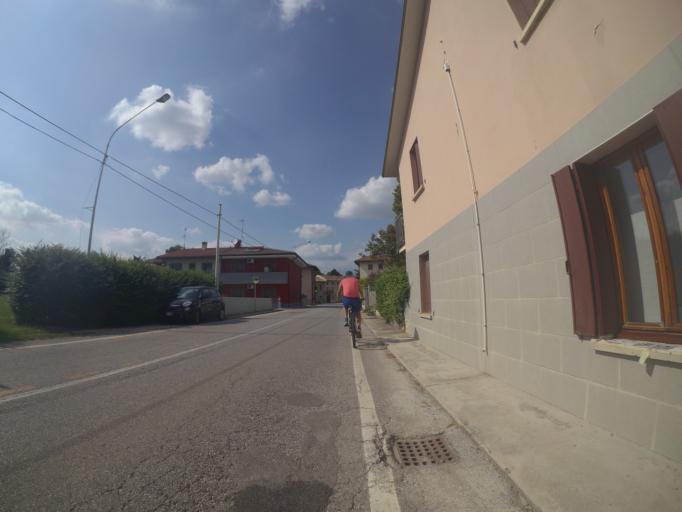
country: IT
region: Friuli Venezia Giulia
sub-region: Provincia di Udine
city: Basiliano-Vissandone
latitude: 46.0550
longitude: 13.0861
